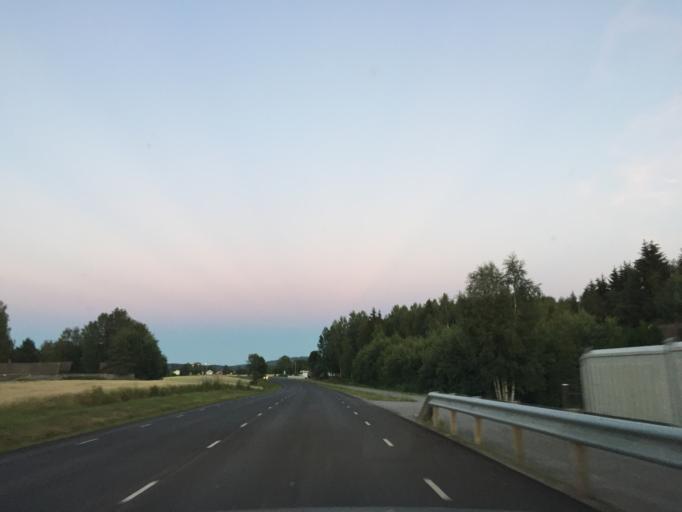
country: NO
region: Hedmark
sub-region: Kongsvinger
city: Spetalen
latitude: 60.2350
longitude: 11.8021
